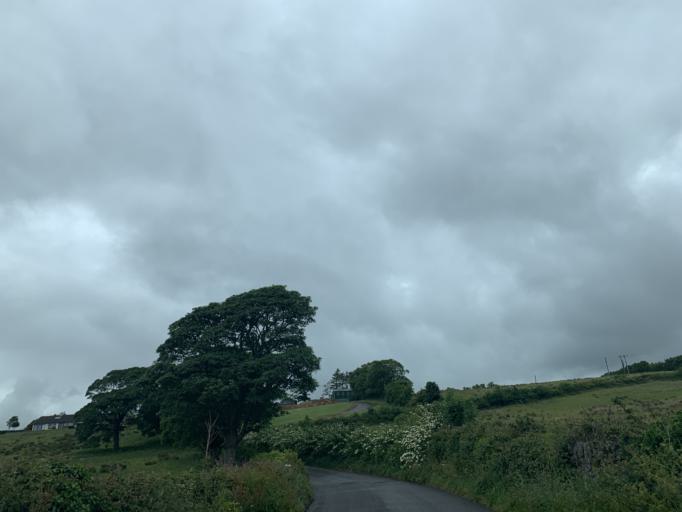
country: IE
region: Connaught
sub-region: Sligo
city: Sligo
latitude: 54.2916
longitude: -8.4636
